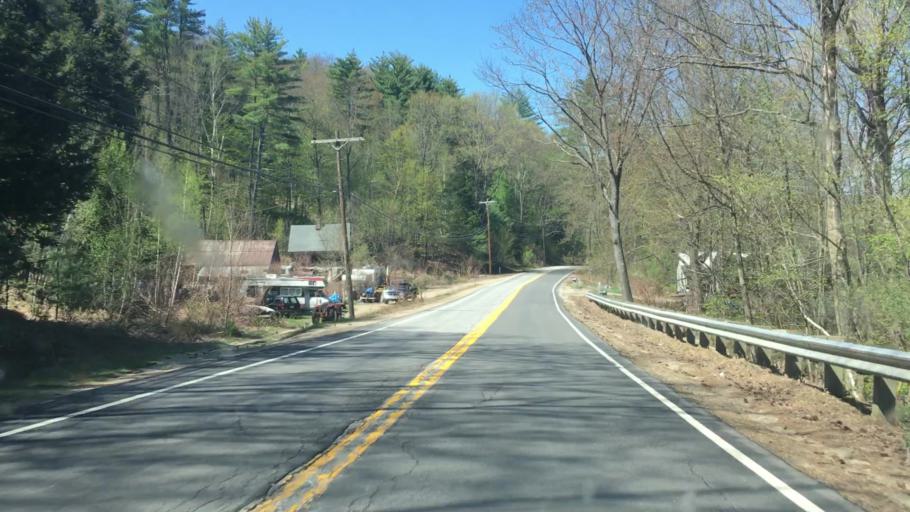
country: US
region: New Hampshire
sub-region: Grafton County
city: Plymouth
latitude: 43.7356
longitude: -71.6763
